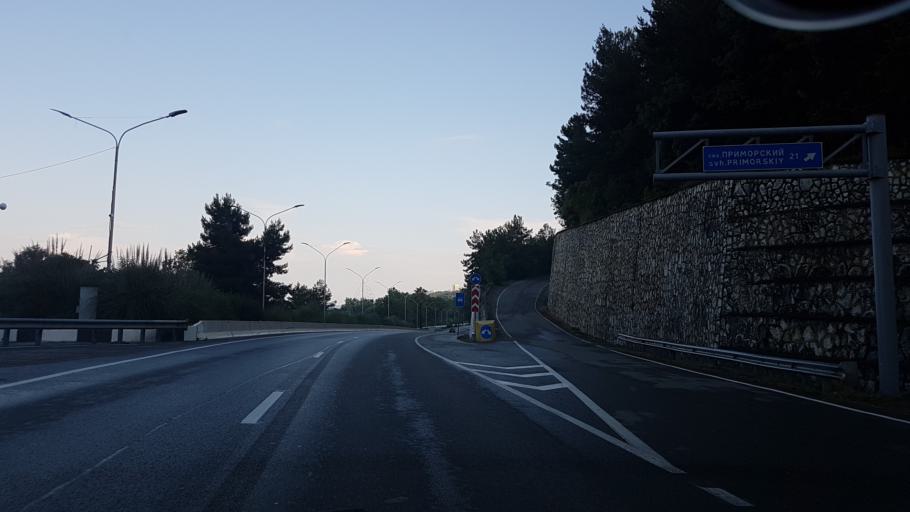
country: RU
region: Krasnodarskiy
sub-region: Sochi City
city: Khosta
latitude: 43.5215
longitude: 39.8432
